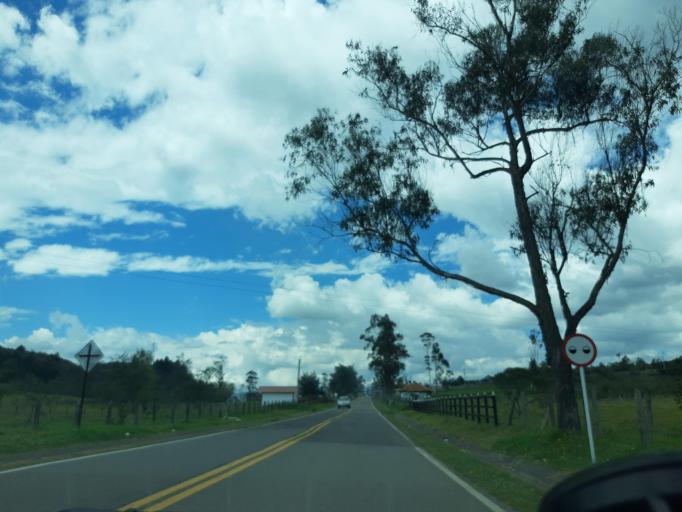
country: CO
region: Boyaca
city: Raquira
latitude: 5.5883
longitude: -73.7107
